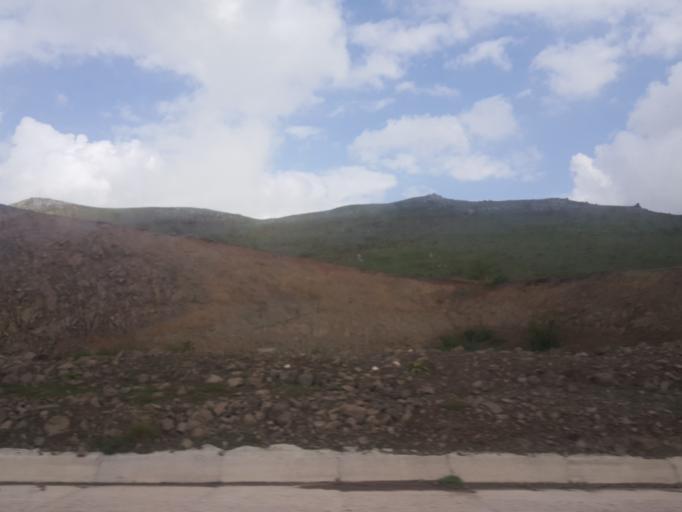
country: TR
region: Tokat
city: Bereketli
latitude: 40.5595
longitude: 37.3078
